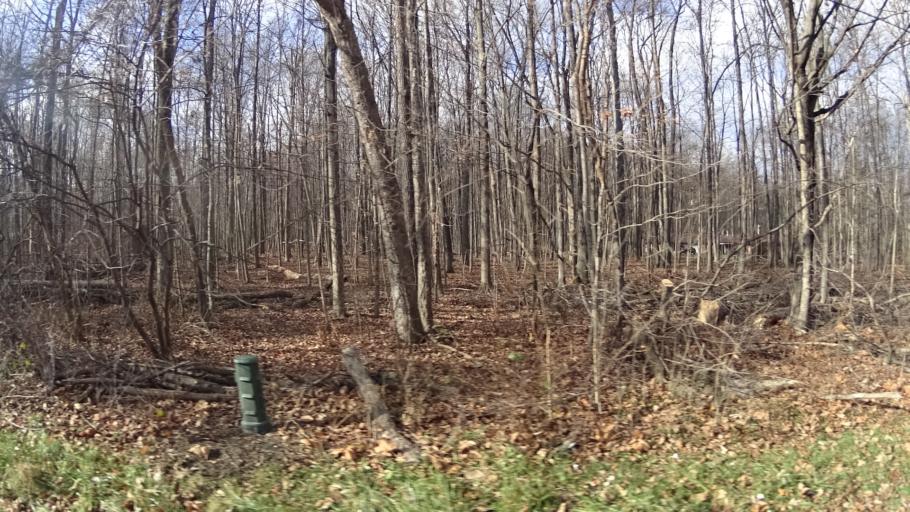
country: US
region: Ohio
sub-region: Lorain County
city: Camden
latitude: 41.2815
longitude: -82.2885
